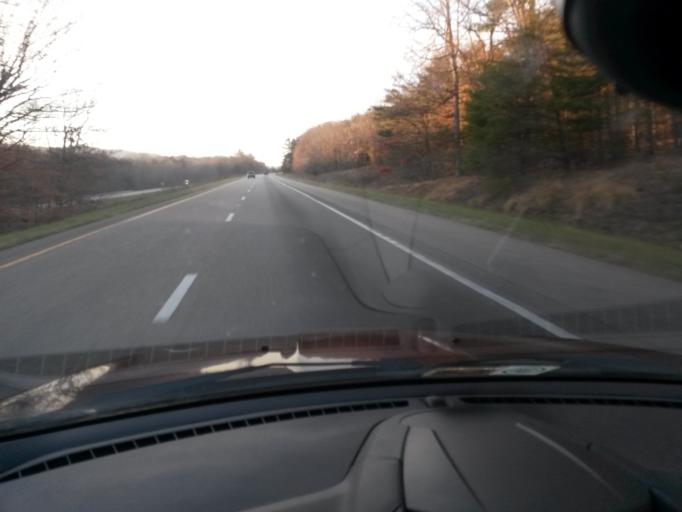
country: US
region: Virginia
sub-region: City of Lexington
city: Lexington
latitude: 37.8776
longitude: -79.5359
